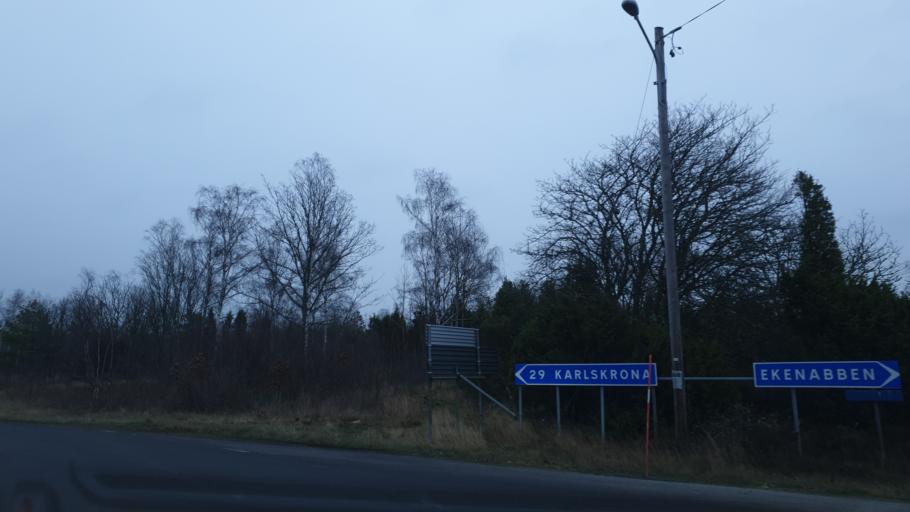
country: SE
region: Blekinge
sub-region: Karlskrona Kommun
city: Sturko
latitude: 56.1070
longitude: 15.6435
